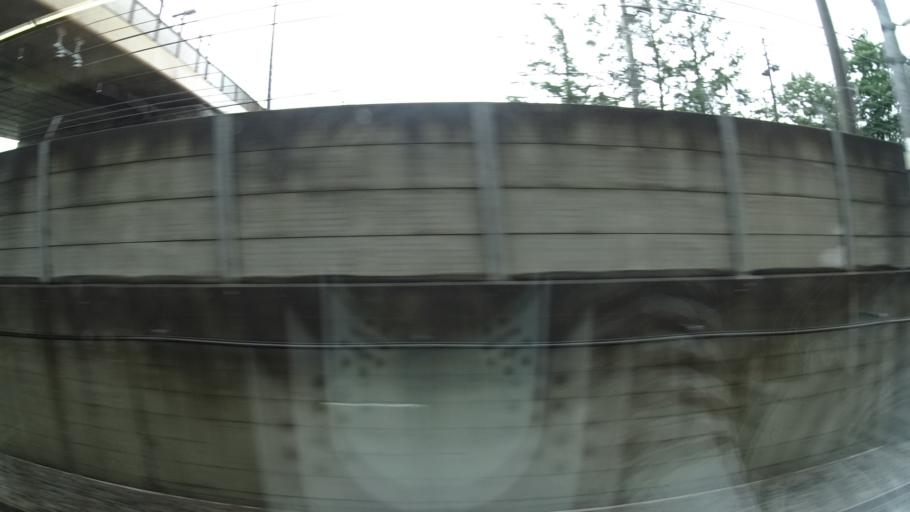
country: JP
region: Nagano
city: Saku
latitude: 36.3428
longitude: 138.6192
